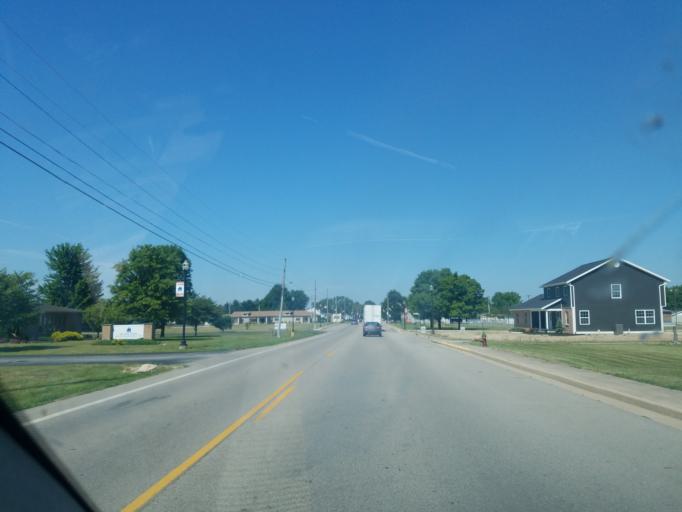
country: US
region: Ohio
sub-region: Shelby County
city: Jackson Center
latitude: 40.4394
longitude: -84.0283
